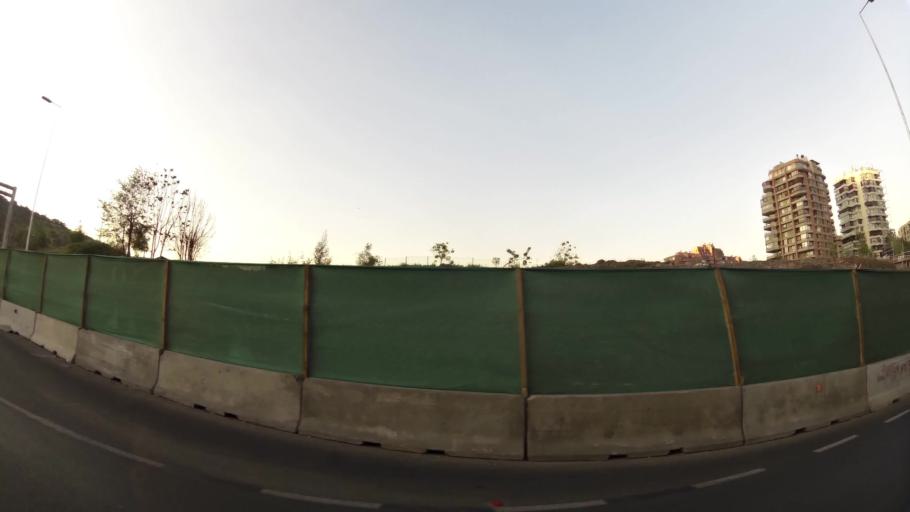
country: CL
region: Santiago Metropolitan
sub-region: Provincia de Santiago
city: Villa Presidente Frei, Nunoa, Santiago, Chile
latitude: -33.4077
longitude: -70.6022
